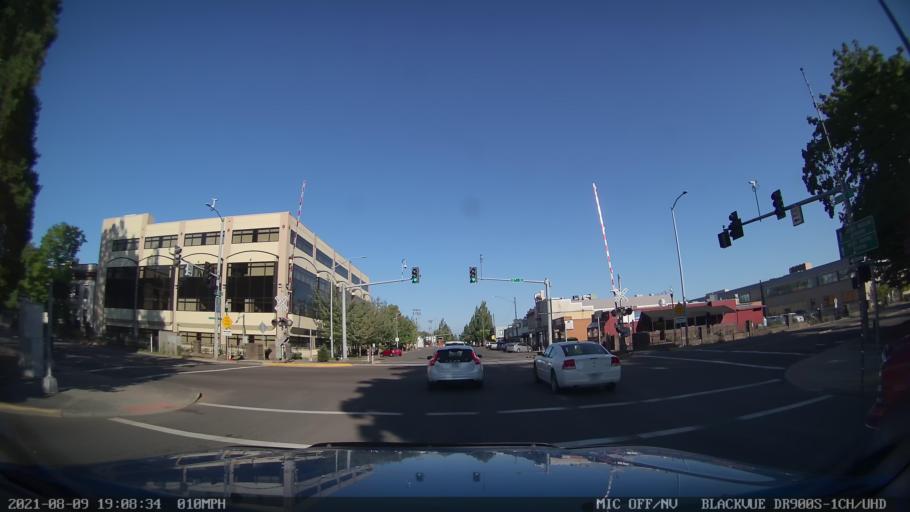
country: US
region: Oregon
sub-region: Marion County
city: Salem
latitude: 44.9371
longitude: -123.0275
